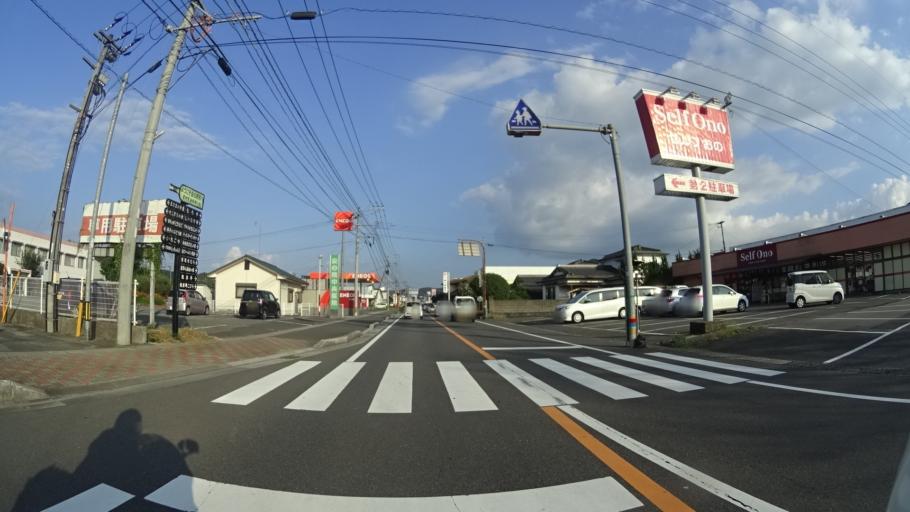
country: JP
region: Oita
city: Bungo-Takada-shi
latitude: 33.4390
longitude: 131.3549
